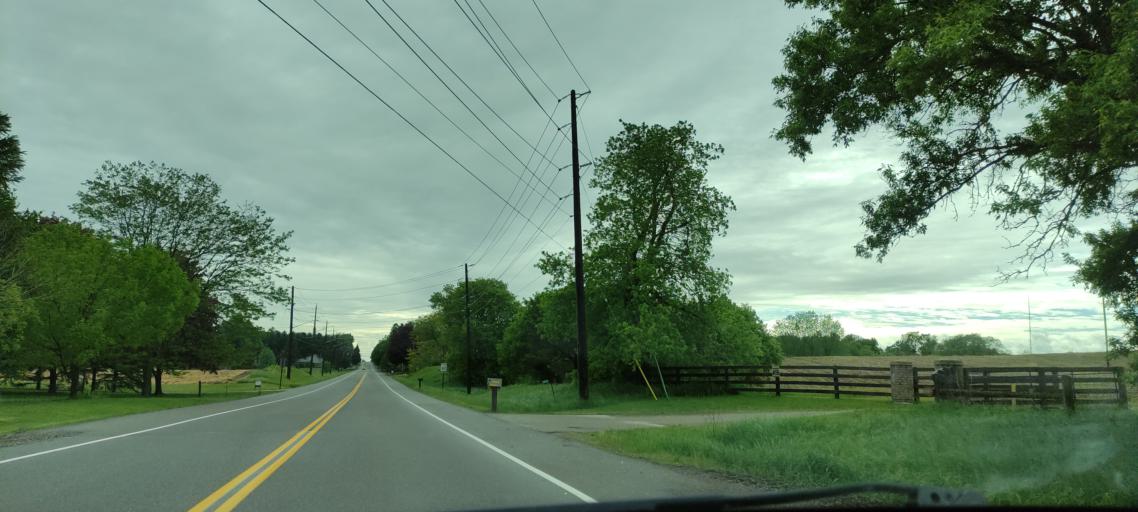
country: CA
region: Ontario
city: Kitchener
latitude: 43.3898
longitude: -80.5994
